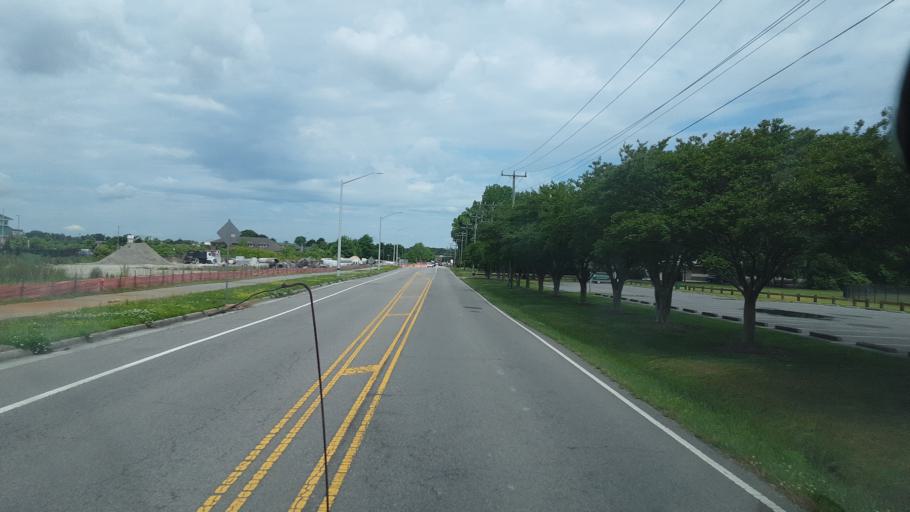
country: US
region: Virginia
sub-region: City of Virginia Beach
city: Virginia Beach
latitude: 36.7477
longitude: -76.0041
